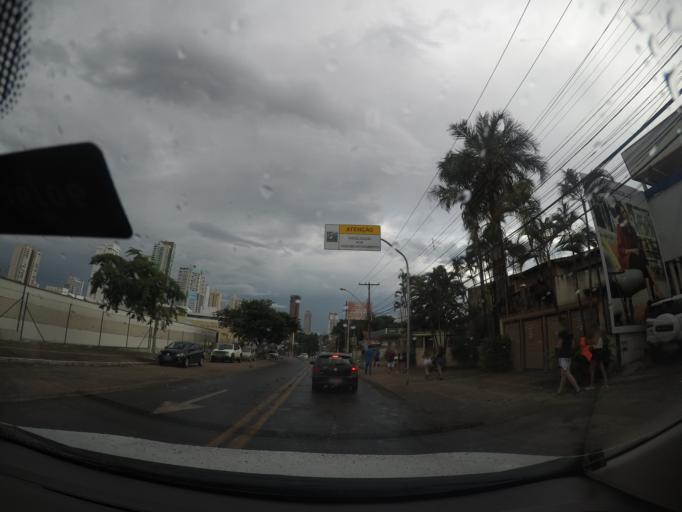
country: BR
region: Goias
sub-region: Goiania
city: Goiania
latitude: -16.7094
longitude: -49.2737
